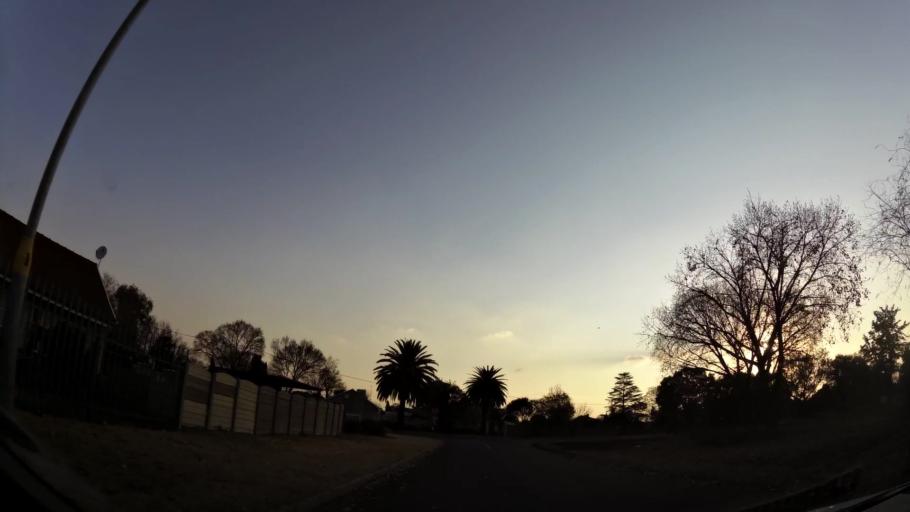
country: ZA
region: Gauteng
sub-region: Ekurhuleni Metropolitan Municipality
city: Springs
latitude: -26.3070
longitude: 28.4509
